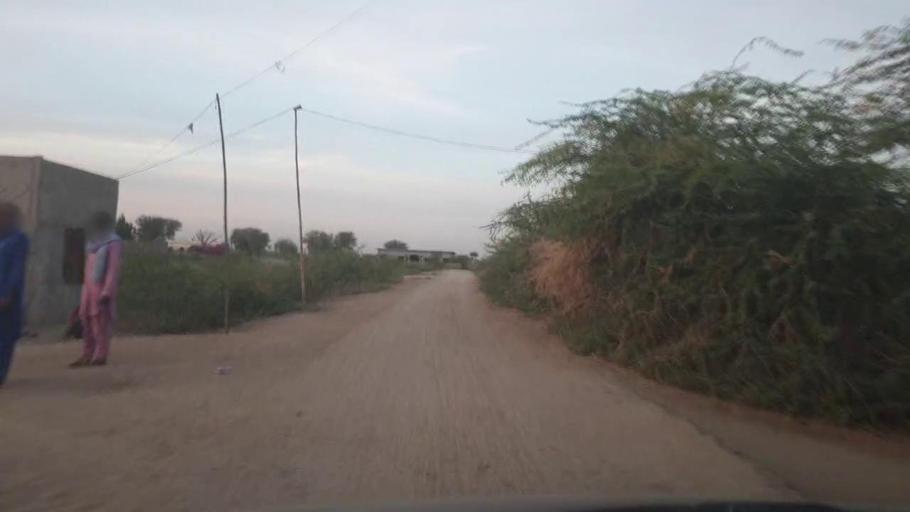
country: PK
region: Sindh
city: Kunri
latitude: 25.2371
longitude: 69.5202
